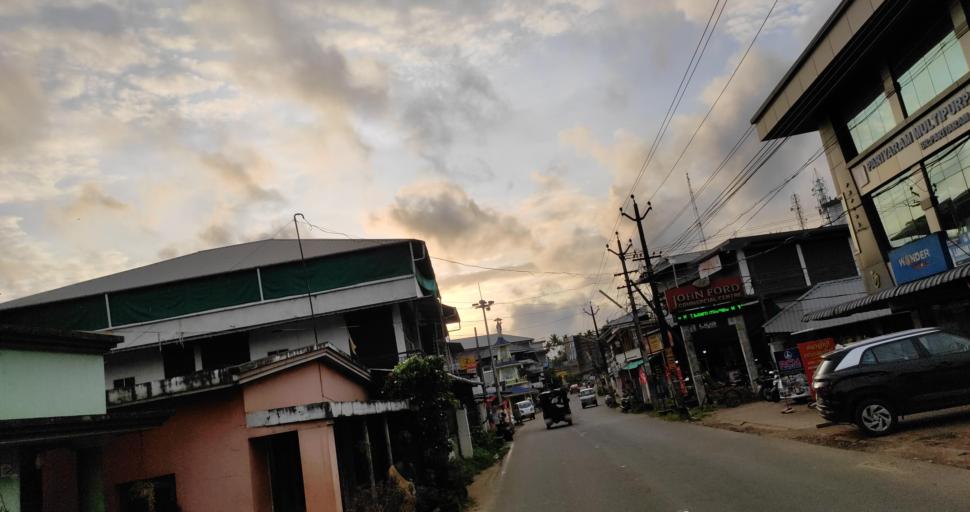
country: IN
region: Kerala
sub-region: Thrissur District
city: Kizhake Chalakudi
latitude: 10.3193
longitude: 76.3723
